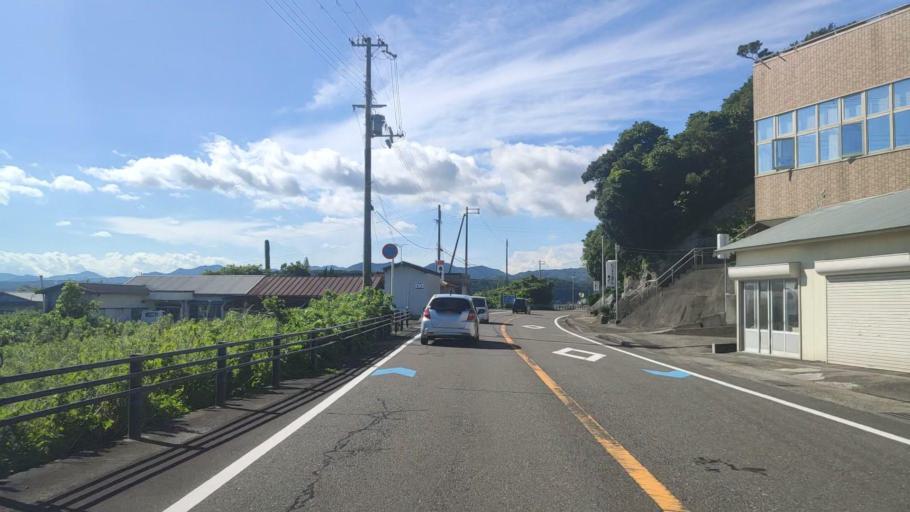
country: JP
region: Wakayama
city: Shingu
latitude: 33.4676
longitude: 135.7753
